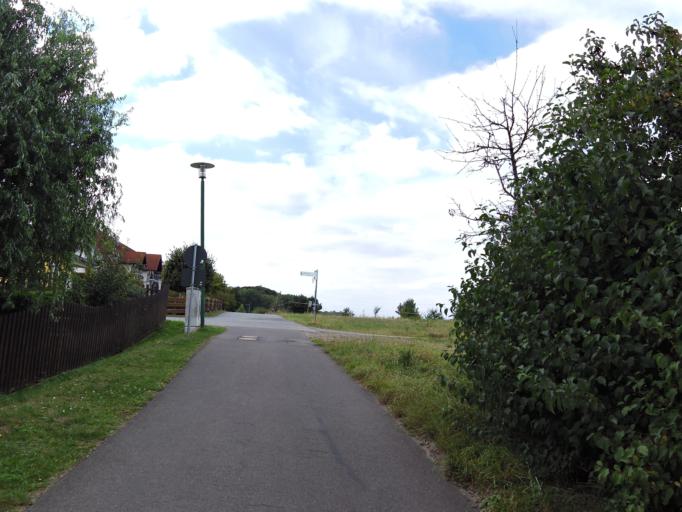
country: DE
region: Saxony
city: Coswig
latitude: 51.1030
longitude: 13.5830
